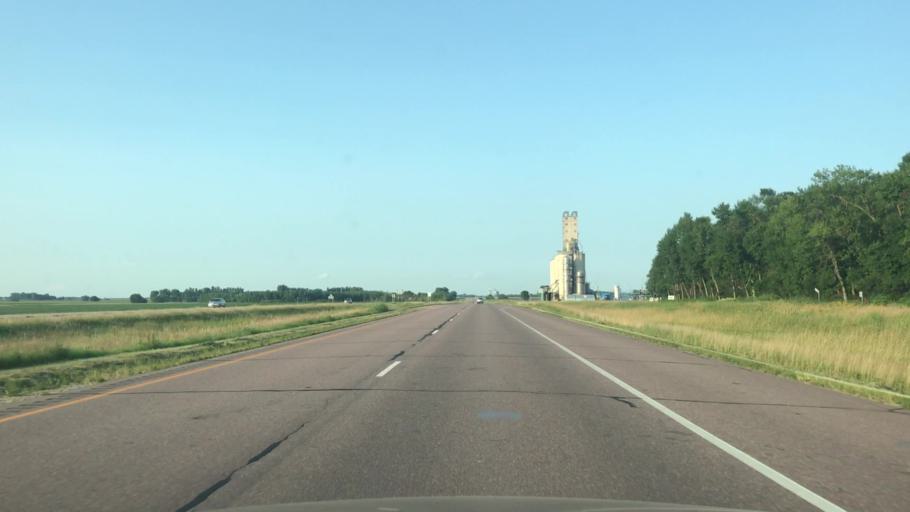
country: US
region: Minnesota
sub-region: Jackson County
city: Lakefield
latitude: 43.7647
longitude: -95.3697
